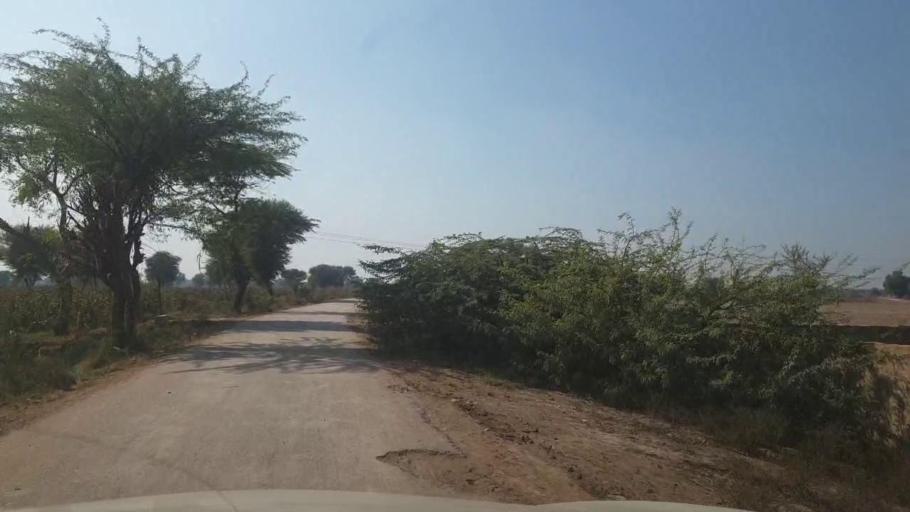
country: PK
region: Sindh
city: Bhan
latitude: 26.5690
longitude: 67.7136
